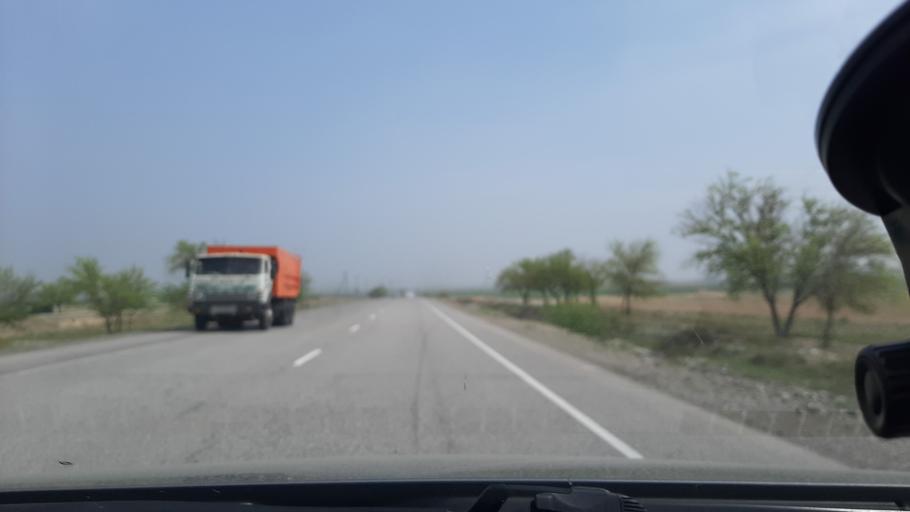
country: UZ
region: Toshkent
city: Bekobod
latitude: 40.1168
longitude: 69.2035
